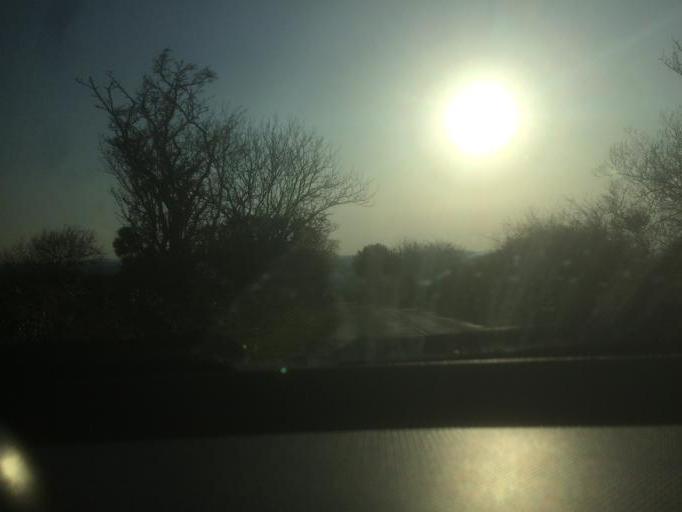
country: GB
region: England
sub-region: Devon
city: Horrabridge
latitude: 50.5584
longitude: -4.0854
